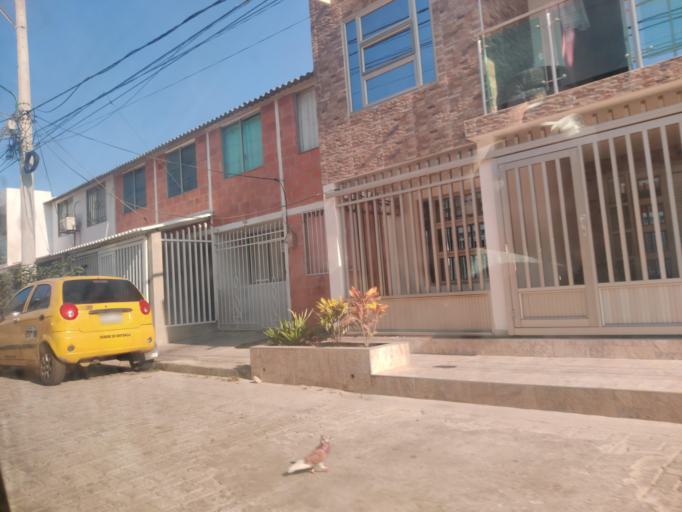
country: CO
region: Atlantico
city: Soledad
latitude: 10.9143
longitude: -74.8136
